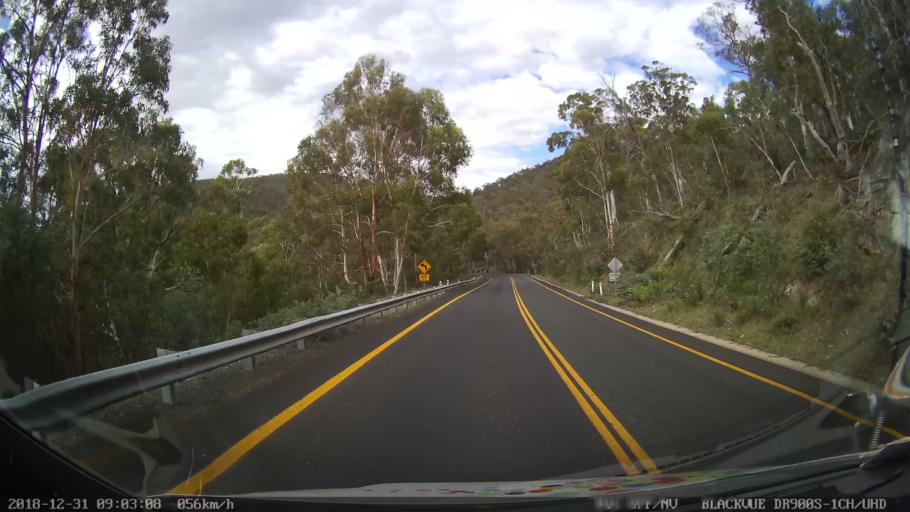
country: AU
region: New South Wales
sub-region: Snowy River
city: Jindabyne
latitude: -36.3456
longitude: 148.5810
